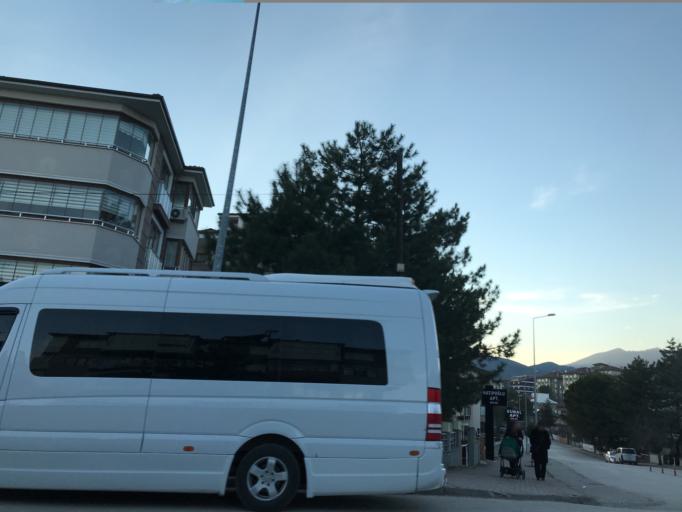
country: TR
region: Karabuk
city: Safranbolu
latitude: 41.2569
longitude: 32.6811
